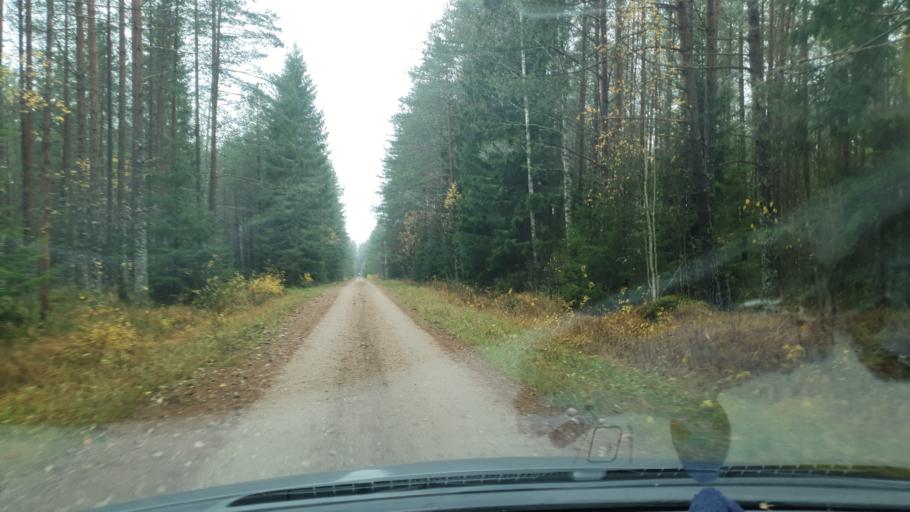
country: EE
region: Viljandimaa
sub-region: Karksi vald
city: Karksi-Nuia
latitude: 57.9758
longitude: 25.6199
